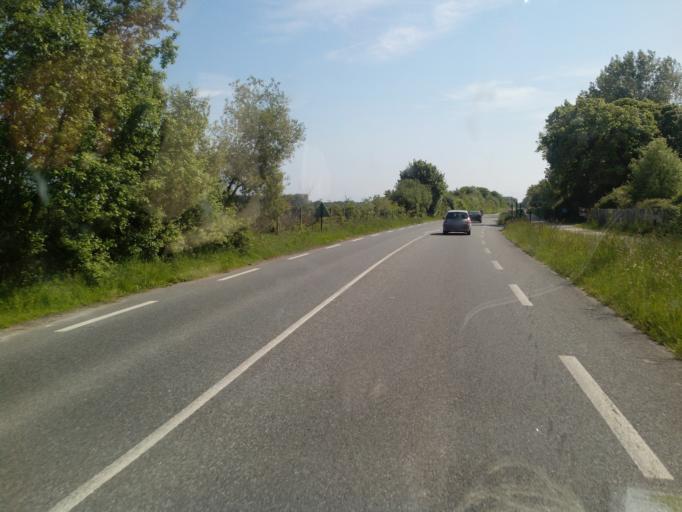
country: FR
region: Nord-Pas-de-Calais
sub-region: Departement du Pas-de-Calais
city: Verton
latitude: 50.3626
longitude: 1.6526
